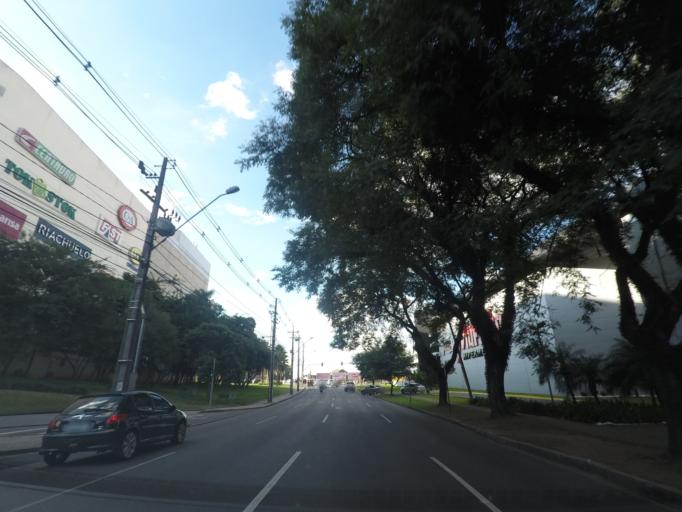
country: BR
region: Parana
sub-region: Curitiba
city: Curitiba
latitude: -25.4781
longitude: -49.2895
